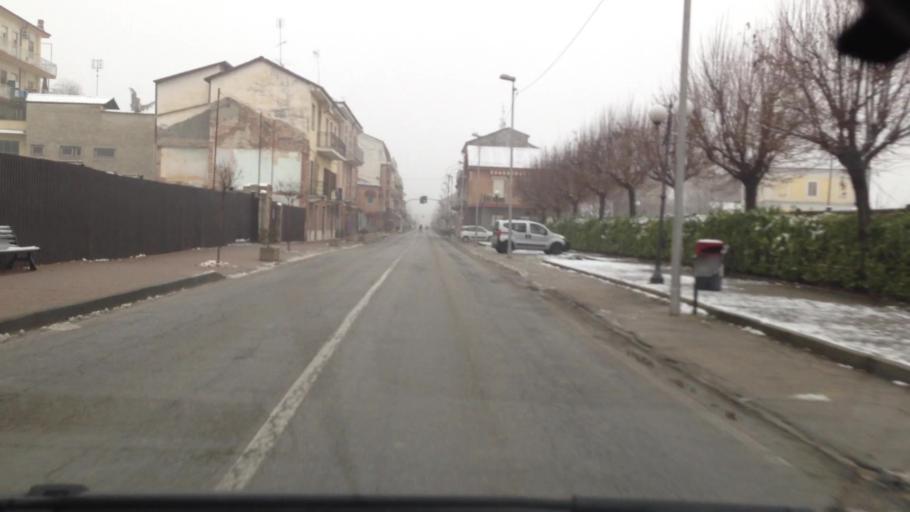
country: IT
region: Piedmont
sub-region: Provincia di Asti
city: Montegrosso
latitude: 44.8196
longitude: 8.2377
